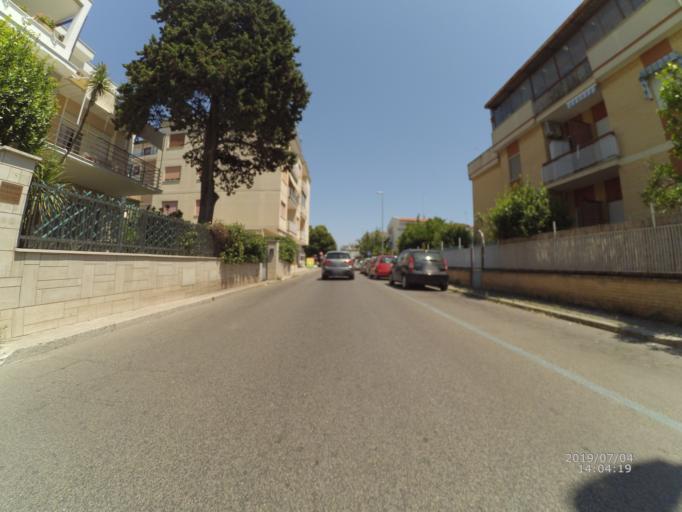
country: IT
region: Latium
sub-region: Provincia di Latina
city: Terracina
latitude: 41.2858
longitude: 13.2447
